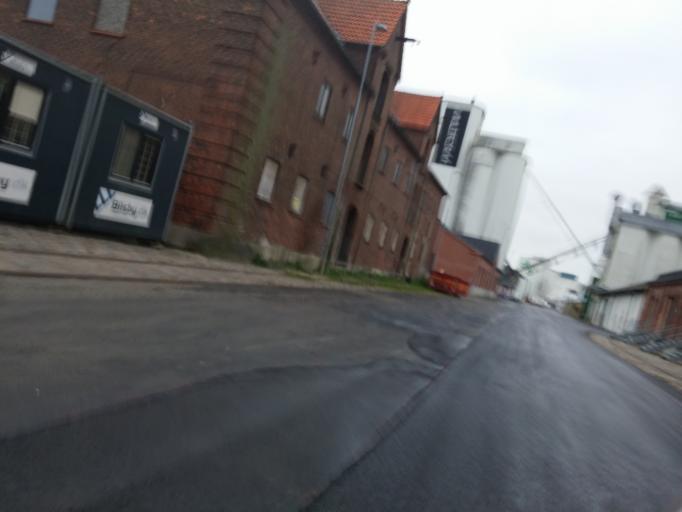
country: DK
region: South Denmark
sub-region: Odense Kommune
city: Odense
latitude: 55.4111
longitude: 10.3826
